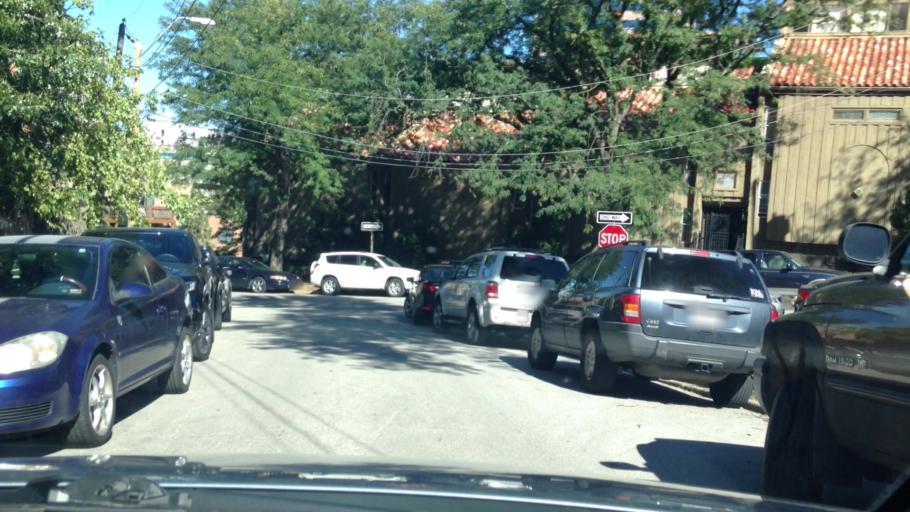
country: US
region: Kansas
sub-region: Johnson County
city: Westwood
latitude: 39.0441
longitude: -94.6012
